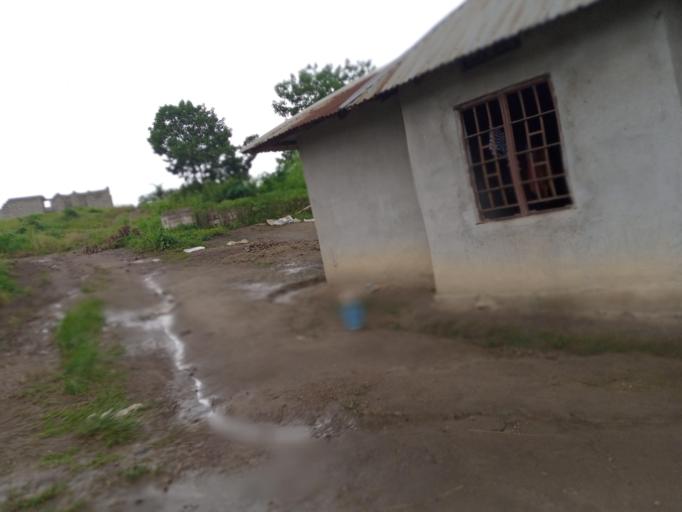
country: SL
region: Eastern Province
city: Kenema
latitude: 7.8588
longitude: -11.1703
